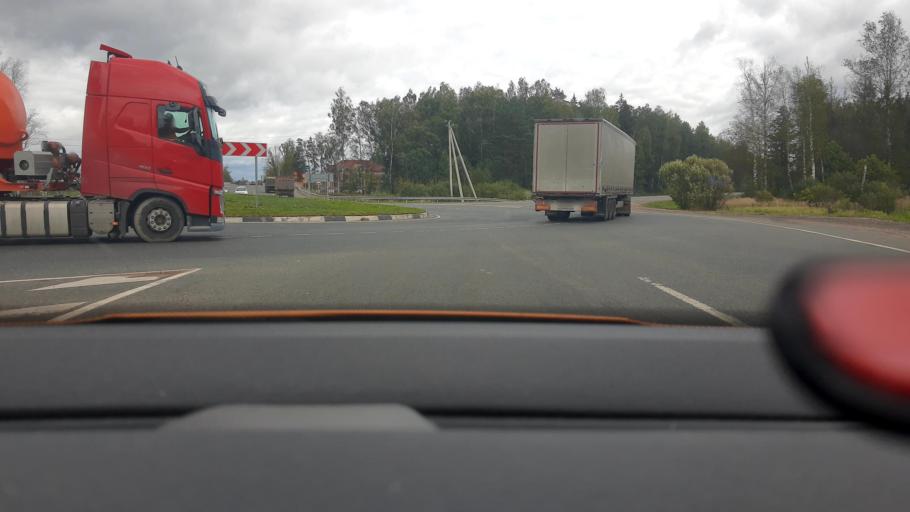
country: RU
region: Moskovskaya
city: Krasnoarmeysk
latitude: 56.0761
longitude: 38.0427
